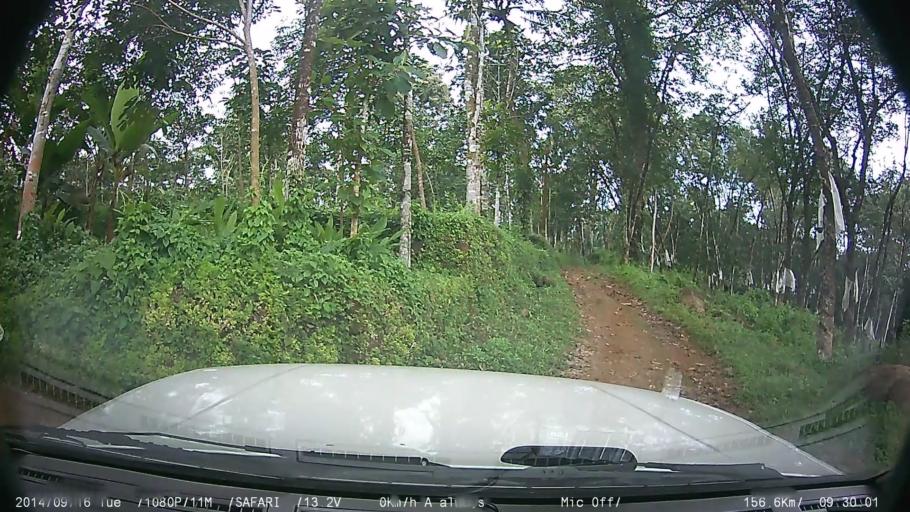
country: IN
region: Kerala
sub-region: Kottayam
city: Palackattumala
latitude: 9.7779
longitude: 76.5577
